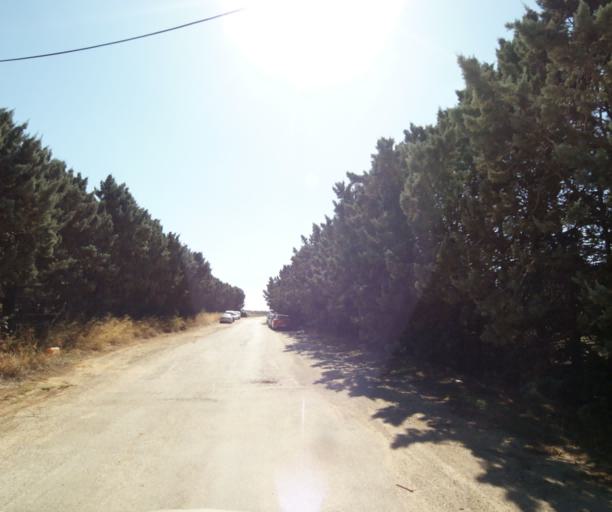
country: FR
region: Languedoc-Roussillon
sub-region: Departement du Gard
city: Rodilhan
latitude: 43.8152
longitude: 4.4217
